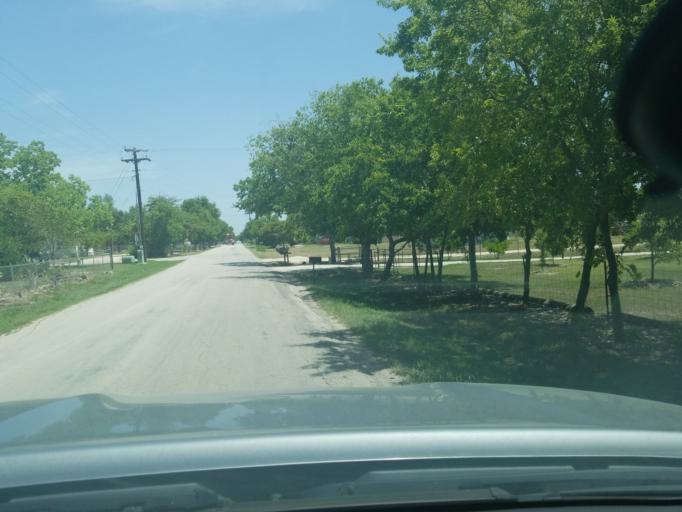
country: US
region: Texas
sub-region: Guadalupe County
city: Cibolo
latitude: 29.5790
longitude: -98.1974
